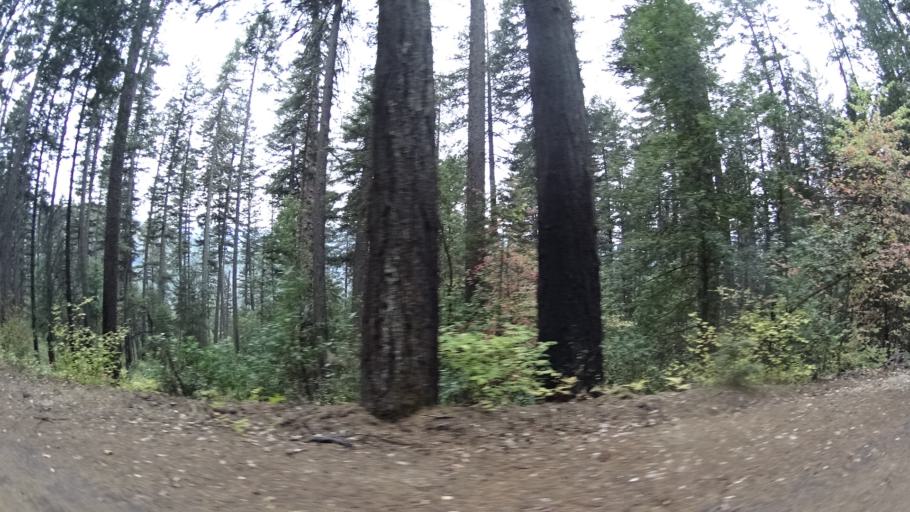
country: US
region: California
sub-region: Siskiyou County
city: Happy Camp
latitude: 41.8042
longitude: -123.3396
